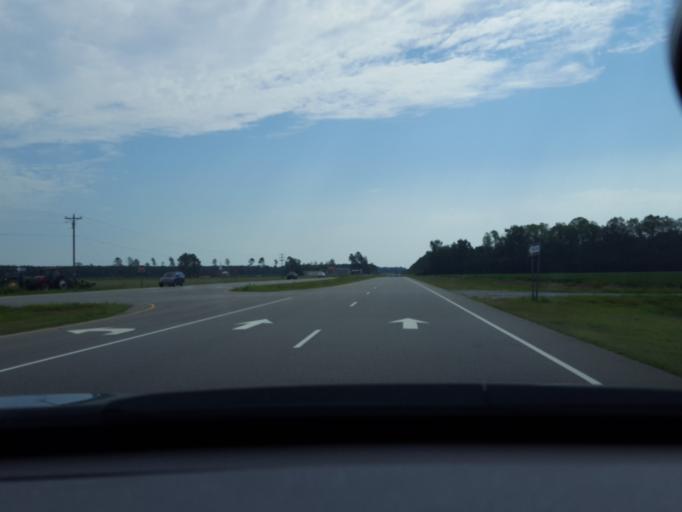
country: US
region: North Carolina
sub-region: Chowan County
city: Edenton
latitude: 36.0390
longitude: -76.7461
